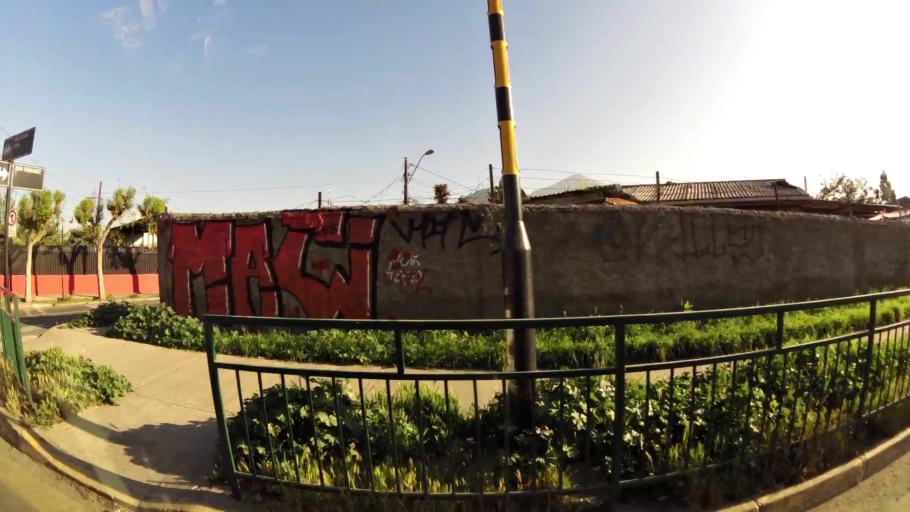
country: CL
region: Santiago Metropolitan
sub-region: Provincia de Santiago
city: Santiago
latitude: -33.3786
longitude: -70.6413
